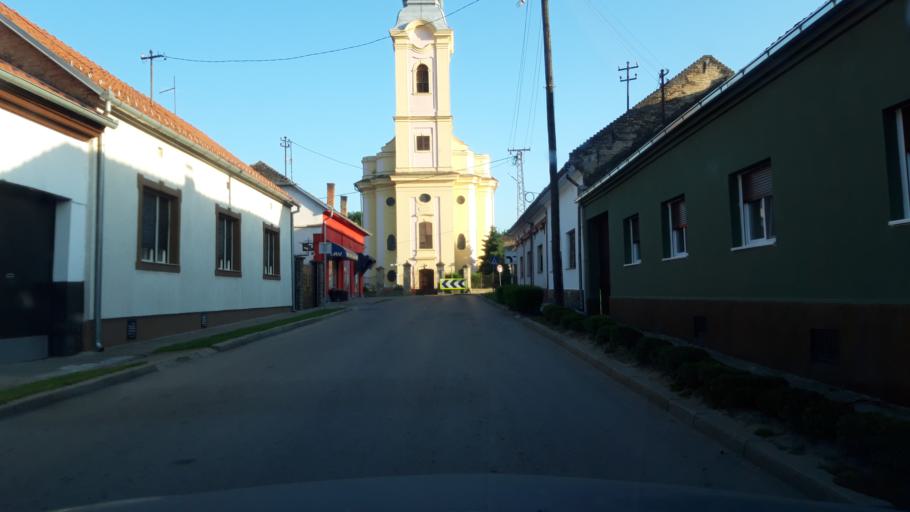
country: RS
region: Autonomna Pokrajina Vojvodina
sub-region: Juznobacki Okrug
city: Beocin
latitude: 45.2195
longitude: 19.6651
